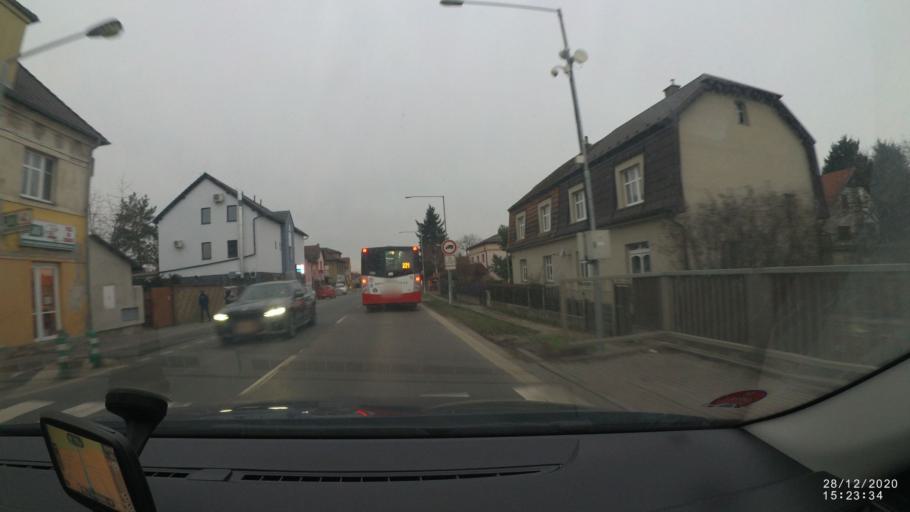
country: CZ
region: Central Bohemia
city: Sestajovice
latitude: 50.0784
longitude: 14.6476
